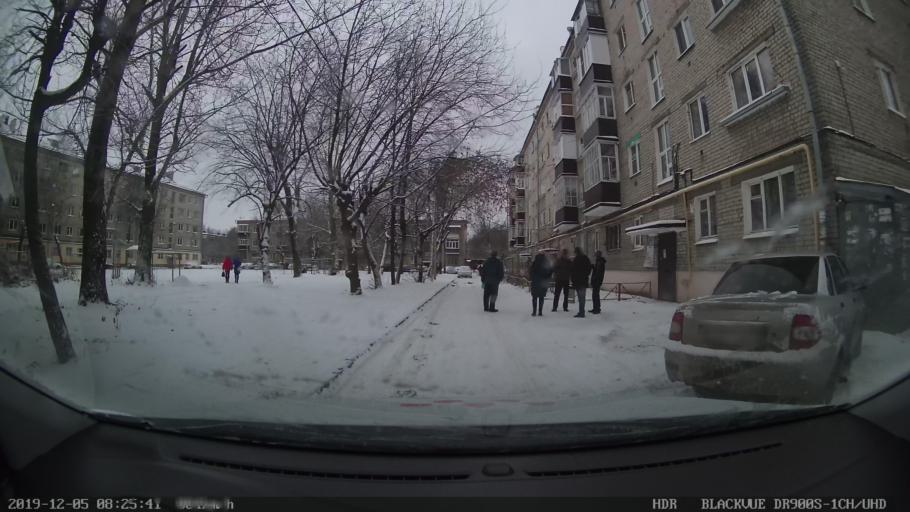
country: RU
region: Tatarstan
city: Staroye Arakchino
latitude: 55.8738
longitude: 49.0208
